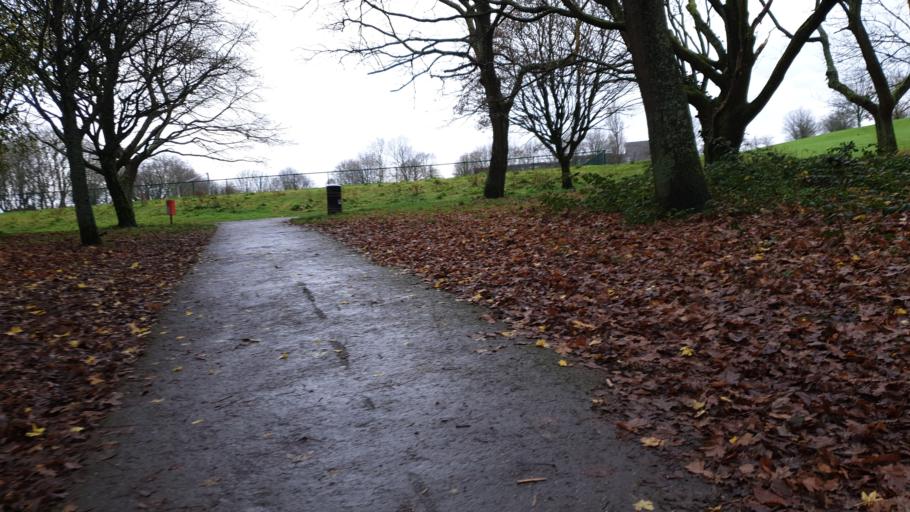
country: IE
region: Munster
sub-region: County Cork
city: Cork
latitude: 51.8915
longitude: -8.4287
